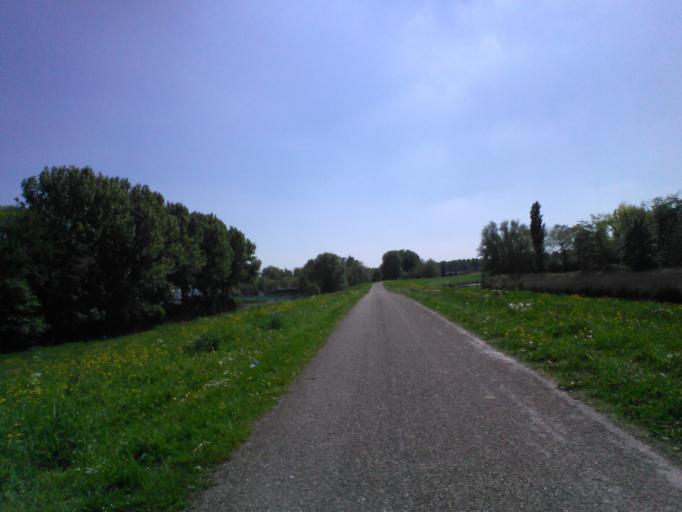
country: NL
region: South Holland
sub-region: Gemeente Papendrecht
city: Papendrecht
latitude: 51.8126
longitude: 4.6977
